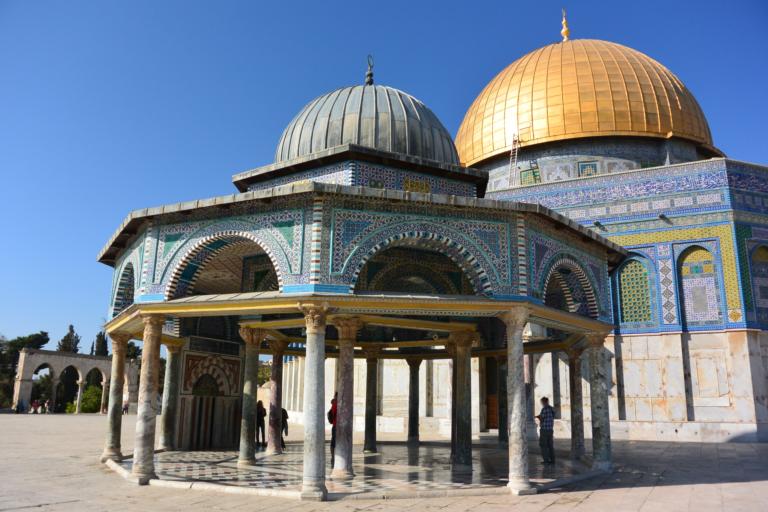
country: PS
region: West Bank
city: Old City
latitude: 31.7782
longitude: 35.2358
